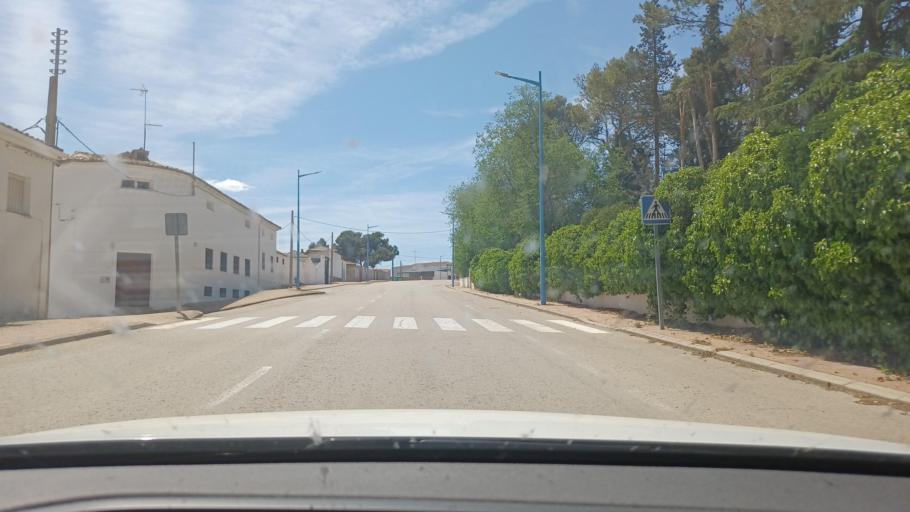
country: ES
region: Castille-La Mancha
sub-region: Provincia de Cuenca
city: Montalbo
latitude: 39.8813
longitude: -2.6716
